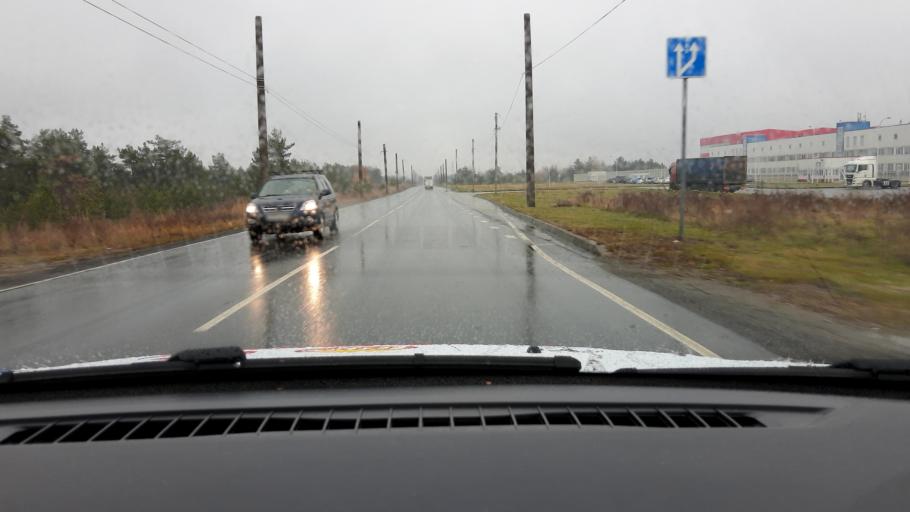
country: RU
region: Nizjnij Novgorod
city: Dzerzhinsk
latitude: 56.2610
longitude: 43.5180
